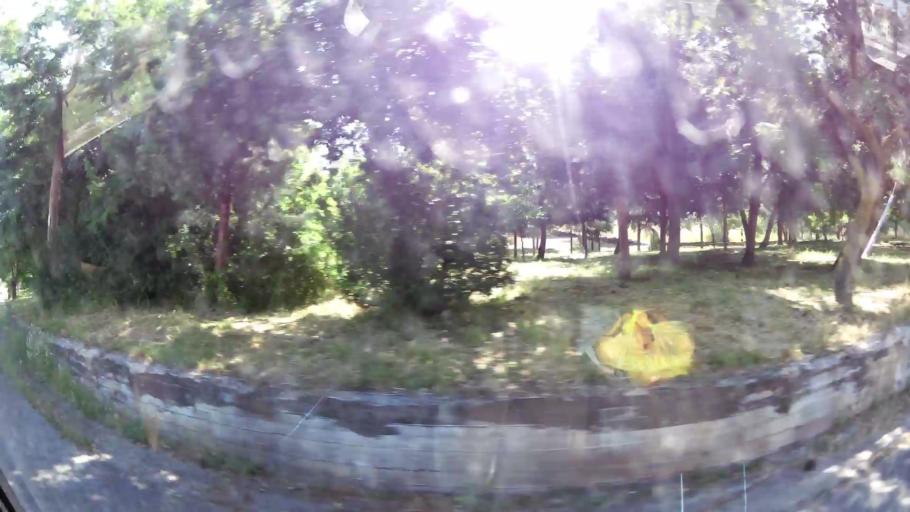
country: GR
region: West Macedonia
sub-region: Nomos Kozanis
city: Koila
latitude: 40.3387
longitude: 21.7879
